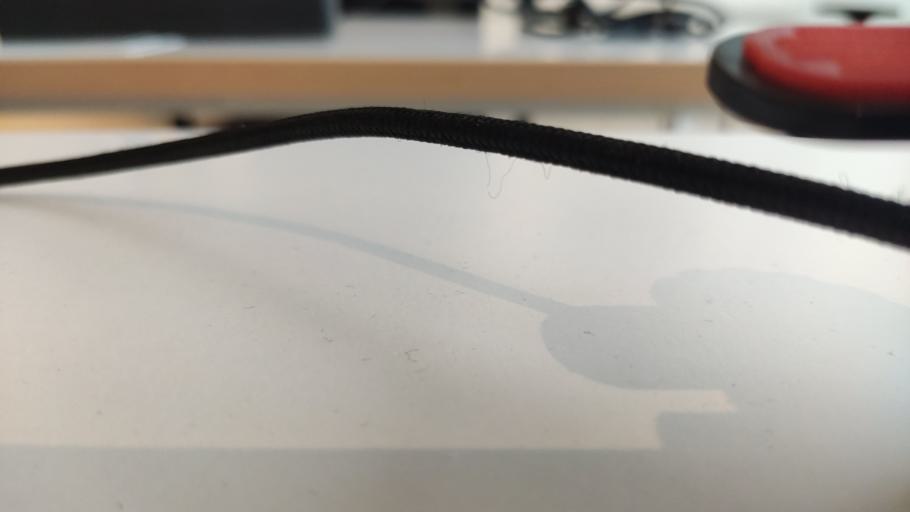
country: RU
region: Moskovskaya
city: Shevlyakovo
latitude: 56.3742
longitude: 36.7965
